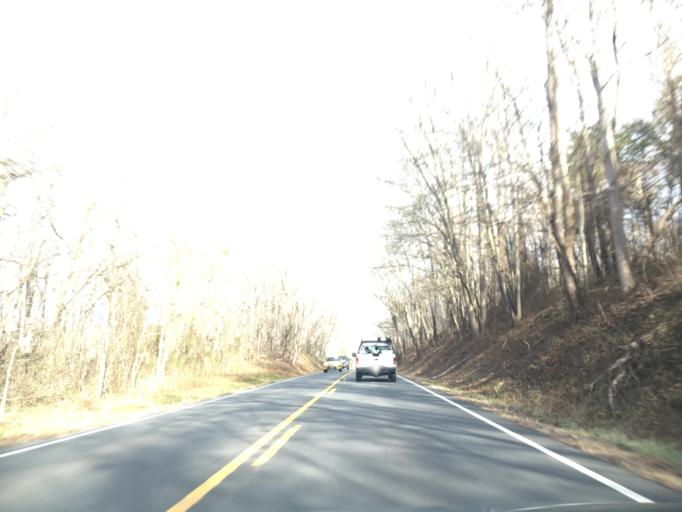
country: US
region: Virginia
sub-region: Culpeper County
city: Culpeper
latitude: 38.6108
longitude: -77.9514
